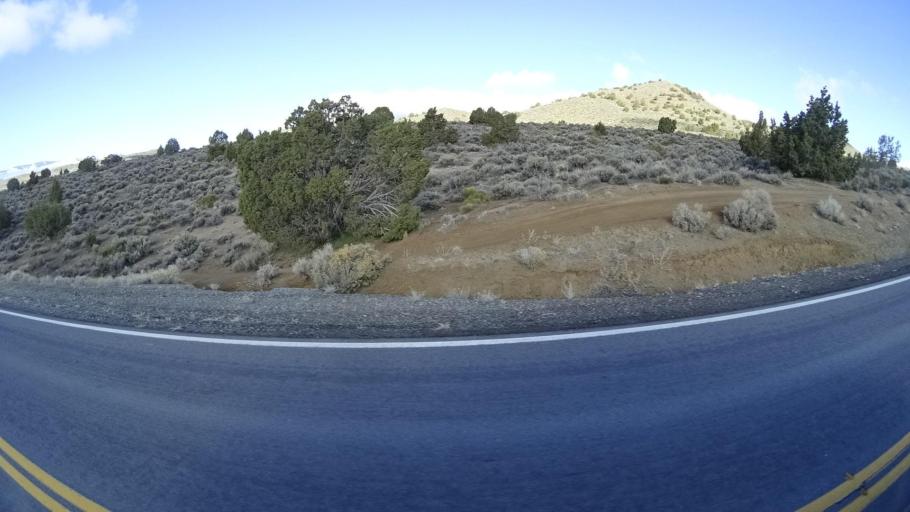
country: US
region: Nevada
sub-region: Washoe County
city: Cold Springs
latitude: 39.7050
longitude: -119.9069
